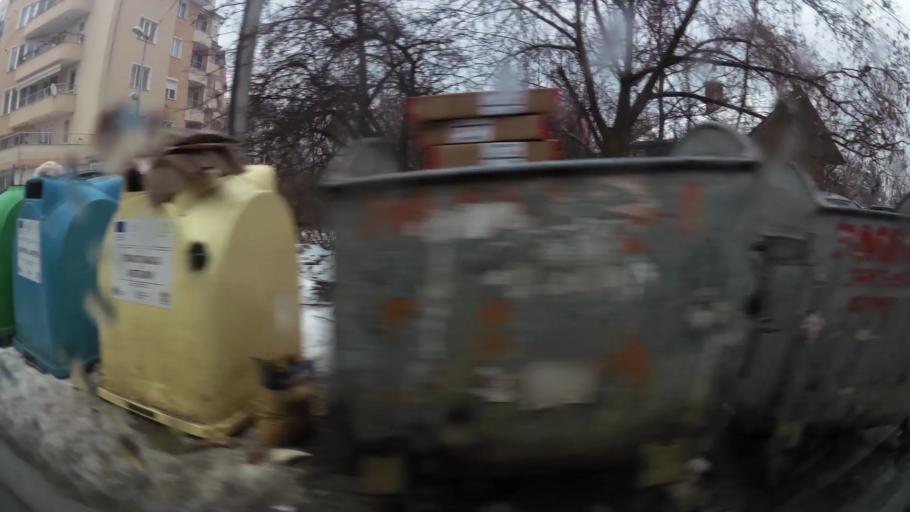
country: BG
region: Sofia-Capital
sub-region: Stolichna Obshtina
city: Sofia
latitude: 42.6779
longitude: 23.2577
